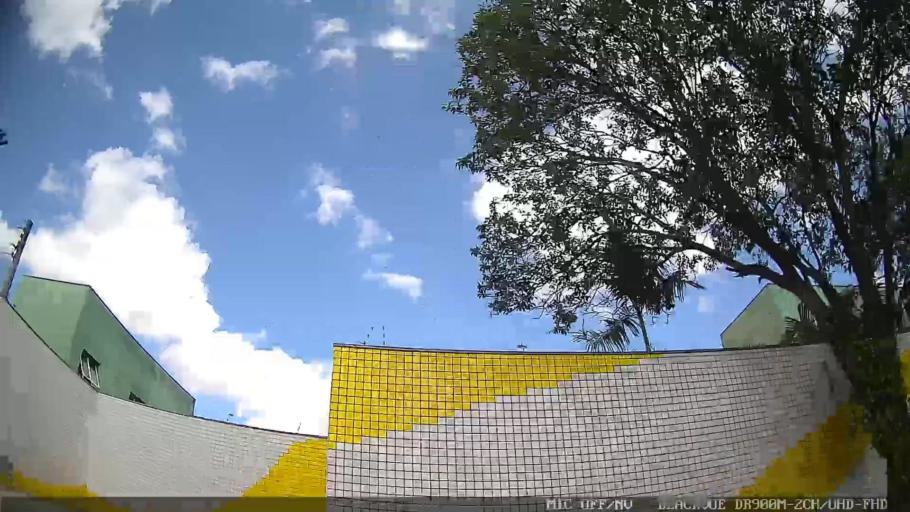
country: BR
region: Sao Paulo
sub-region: Diadema
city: Diadema
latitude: -23.6599
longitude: -46.6043
